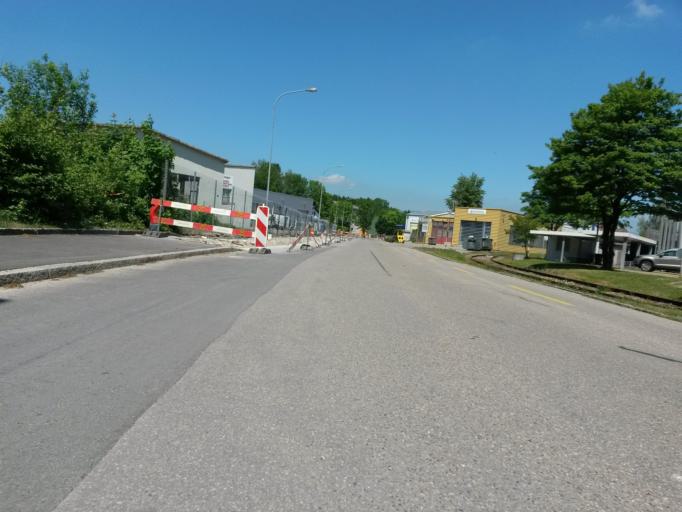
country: CH
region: Bern
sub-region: Seeland District
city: Lyss
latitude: 47.0845
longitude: 7.3036
